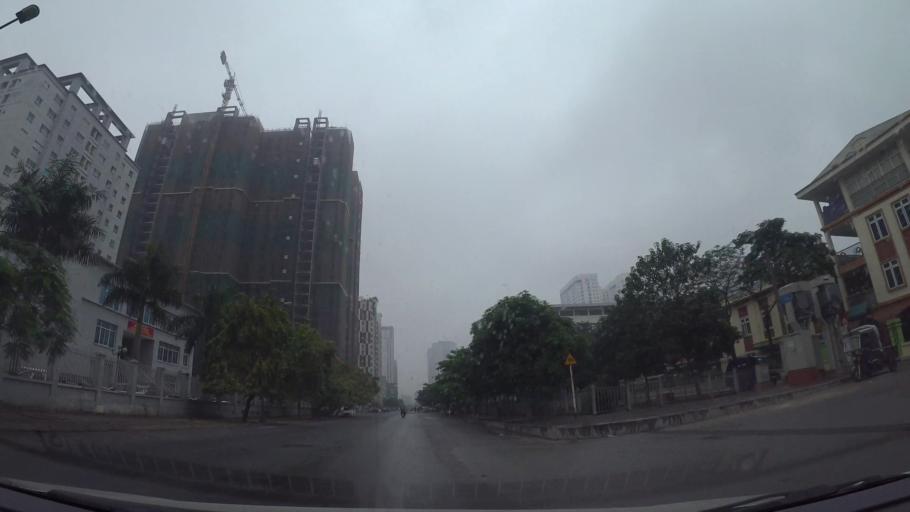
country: VN
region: Ha Noi
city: Cau Giay
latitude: 21.0205
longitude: 105.7953
